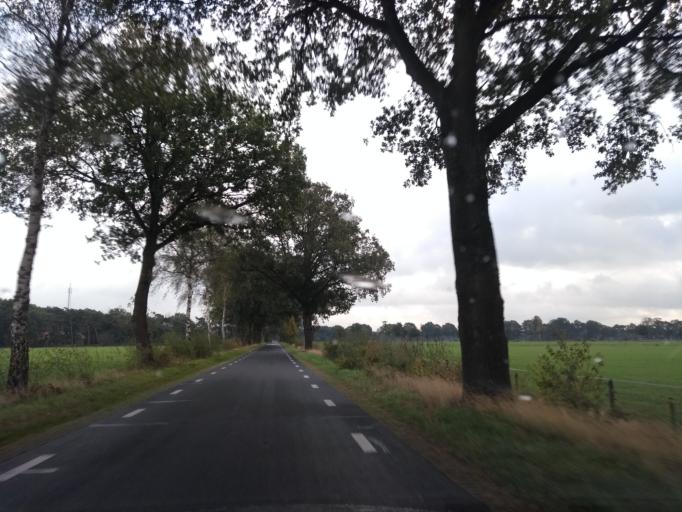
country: NL
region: Gelderland
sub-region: Gemeente Bronckhorst
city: Zelhem
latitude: 52.0279
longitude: 6.3561
